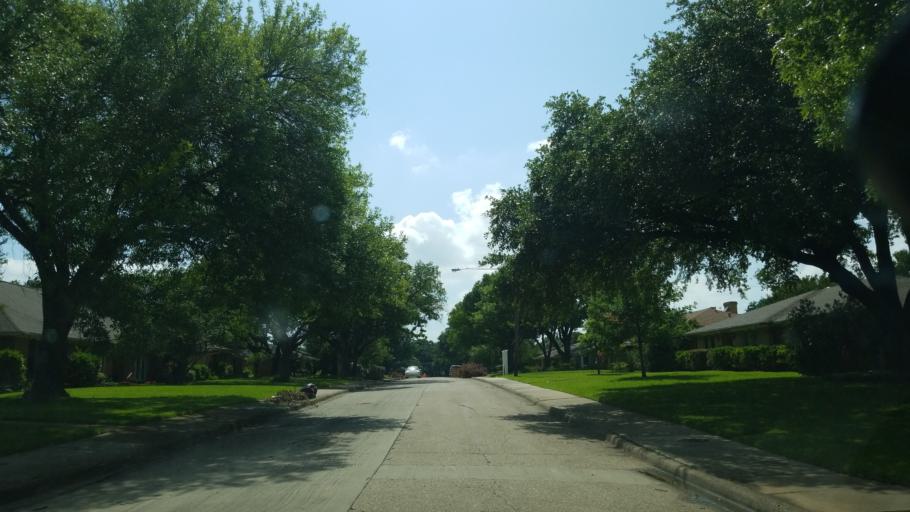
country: US
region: Texas
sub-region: Dallas County
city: Farmers Branch
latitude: 32.8821
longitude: -96.8628
